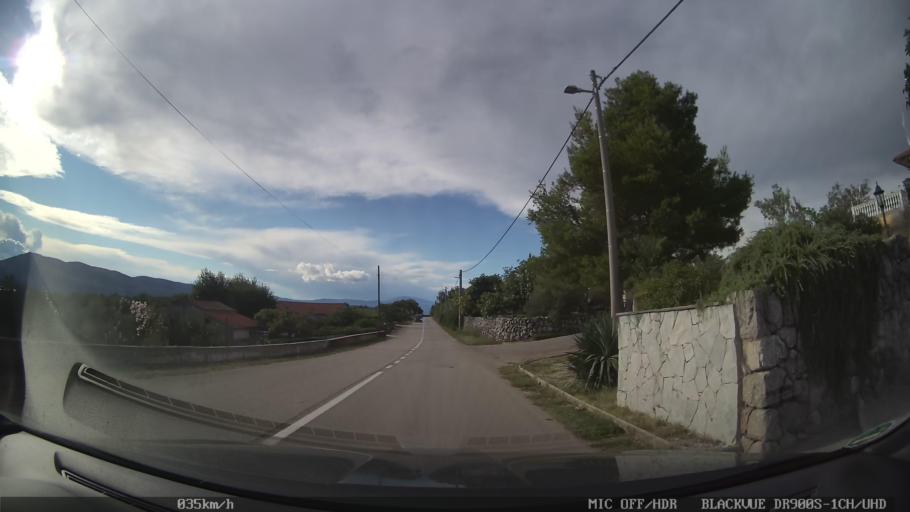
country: HR
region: Primorsko-Goranska
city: Njivice
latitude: 45.0752
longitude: 14.4633
